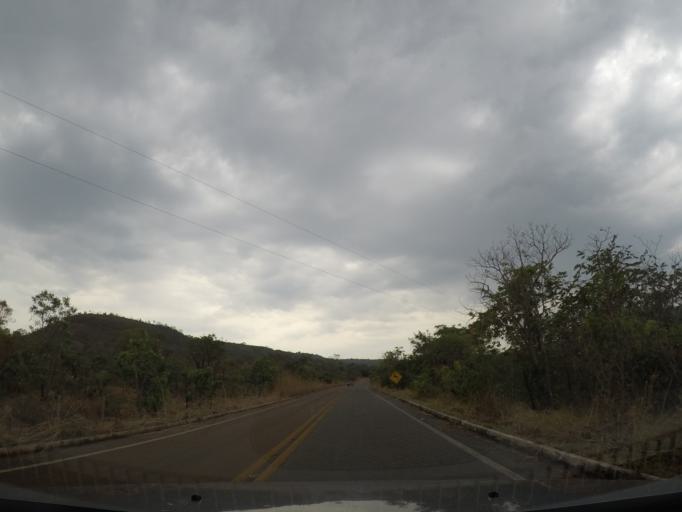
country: BR
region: Goias
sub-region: Pirenopolis
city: Pirenopolis
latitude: -15.8457
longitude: -48.9203
